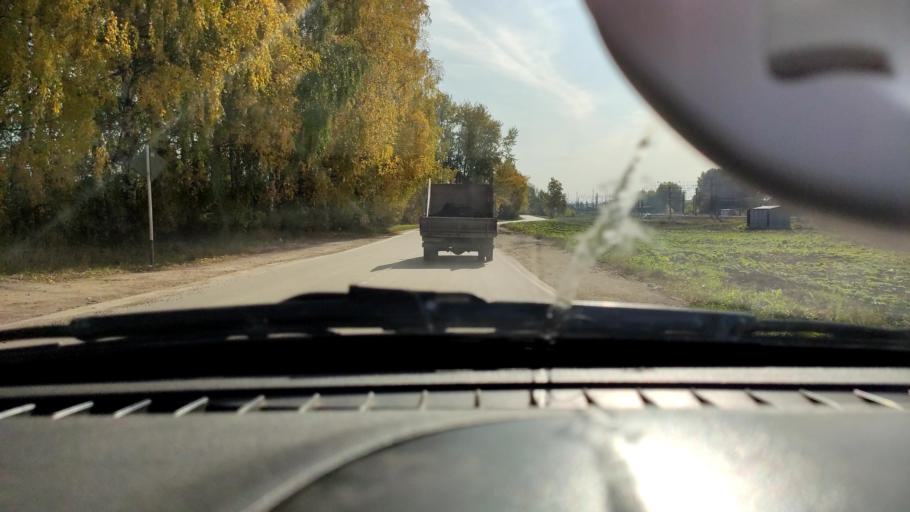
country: RU
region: Perm
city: Overyata
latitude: 58.0935
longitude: 55.8615
